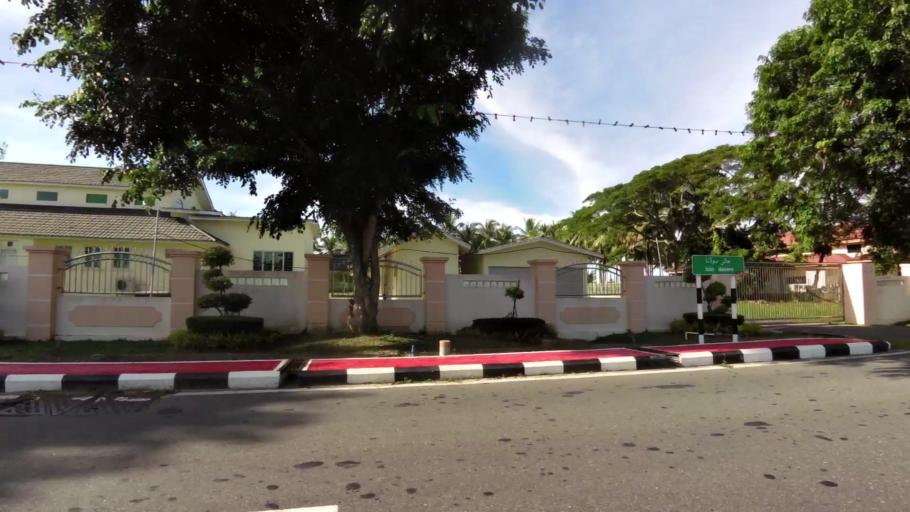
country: BN
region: Belait
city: Kuala Belait
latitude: 4.5885
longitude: 114.1913
